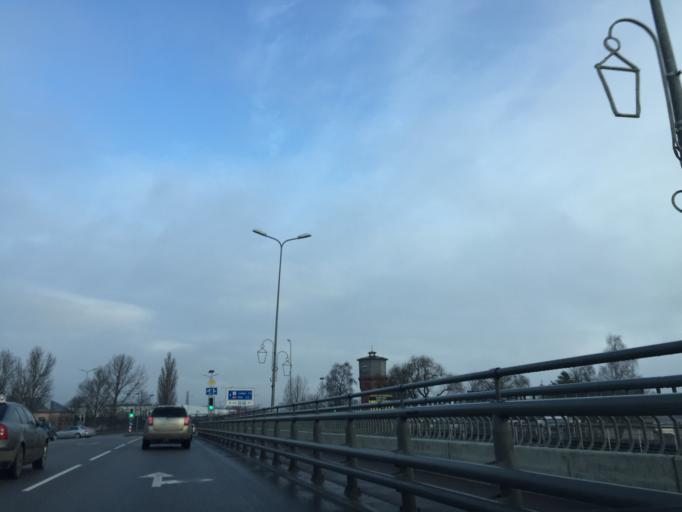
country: LV
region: Liepaja
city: Liepaja
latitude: 56.5129
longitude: 21.0222
